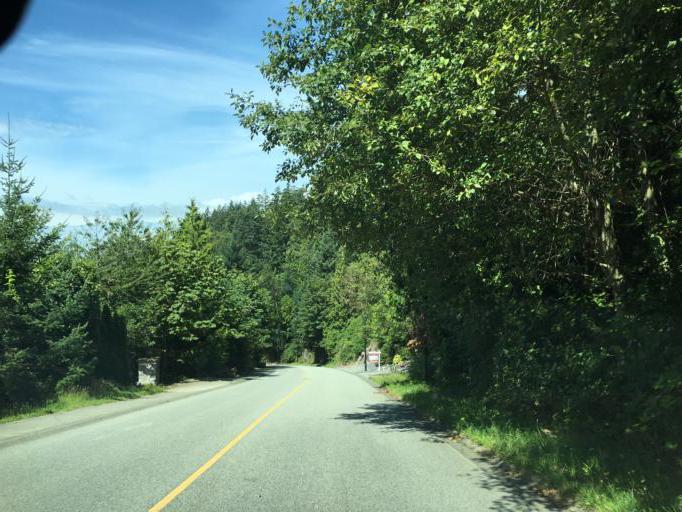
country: CA
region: British Columbia
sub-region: Greater Vancouver Regional District
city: Bowen Island
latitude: 49.3422
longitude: -123.2577
